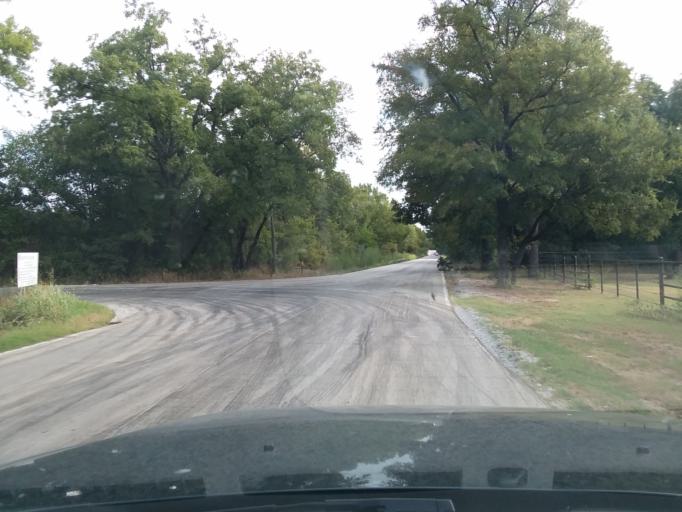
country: US
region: Texas
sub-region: Denton County
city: Copper Canyon
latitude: 33.1247
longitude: -97.1088
